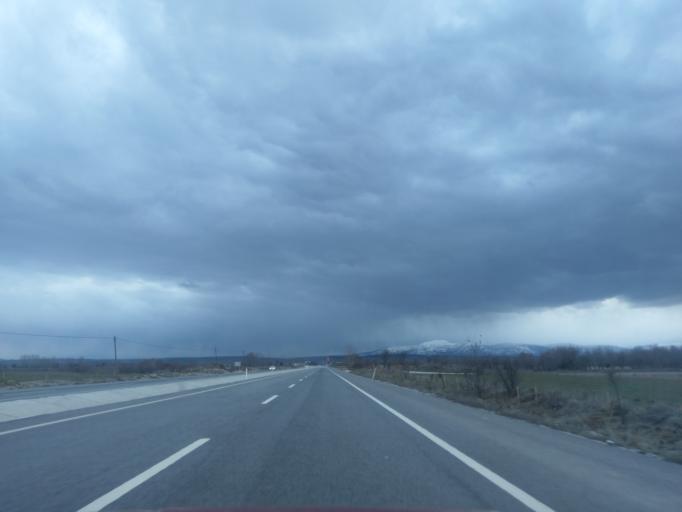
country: TR
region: Kuetahya
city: Cavdarhisar
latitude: 39.2094
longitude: 29.6453
